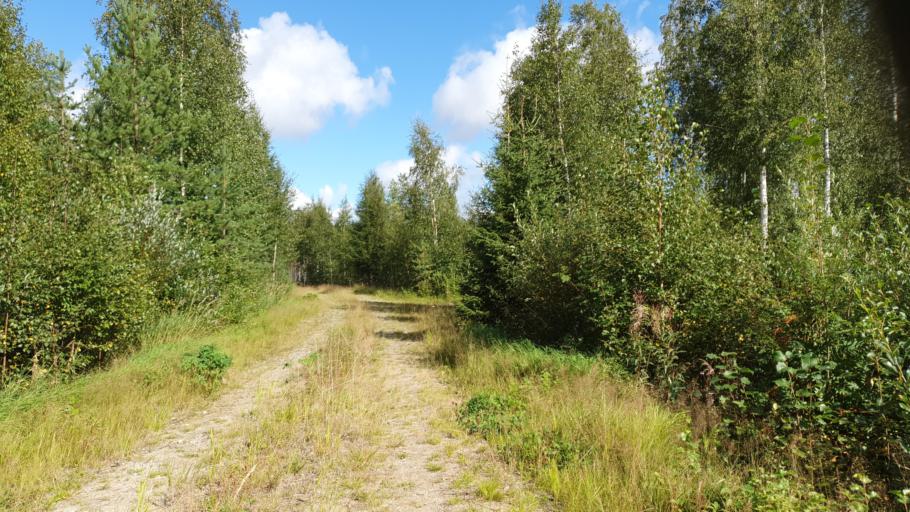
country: FI
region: Kainuu
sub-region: Kehys-Kainuu
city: Kuhmo
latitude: 64.1463
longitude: 29.3549
